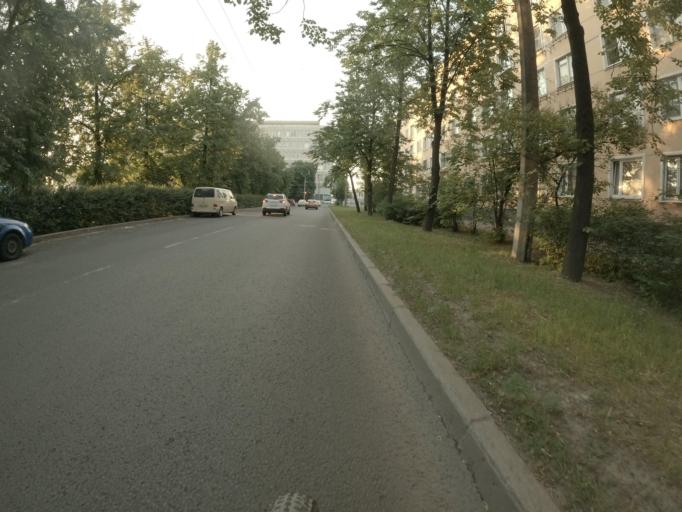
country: RU
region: St.-Petersburg
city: Dachnoye
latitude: 59.8535
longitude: 30.2691
